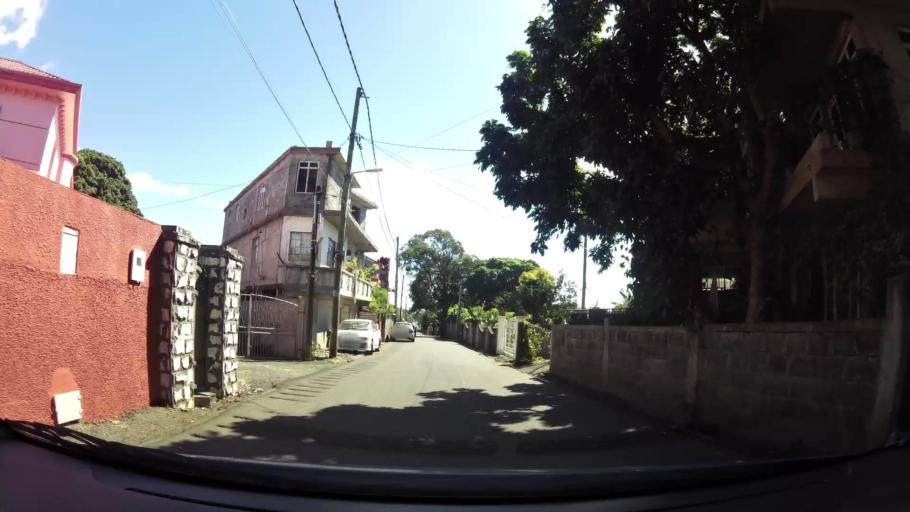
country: MU
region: Plaines Wilhems
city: Vacoas
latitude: -20.2945
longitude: 57.4824
